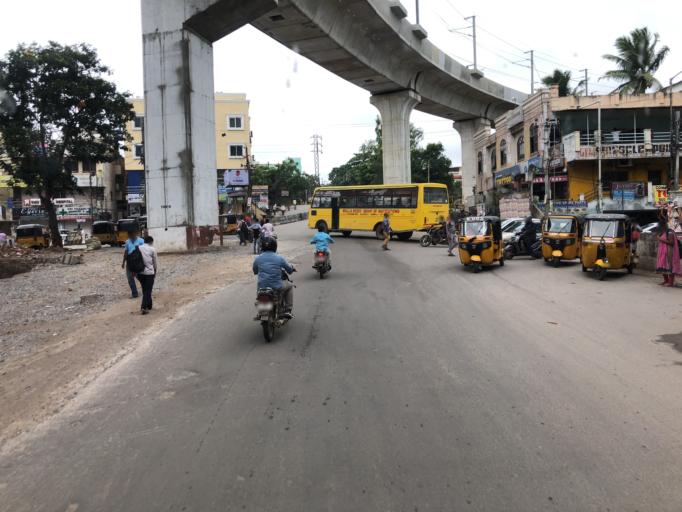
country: IN
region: Telangana
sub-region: Rangareddi
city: Kukatpalli
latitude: 17.4305
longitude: 78.4254
